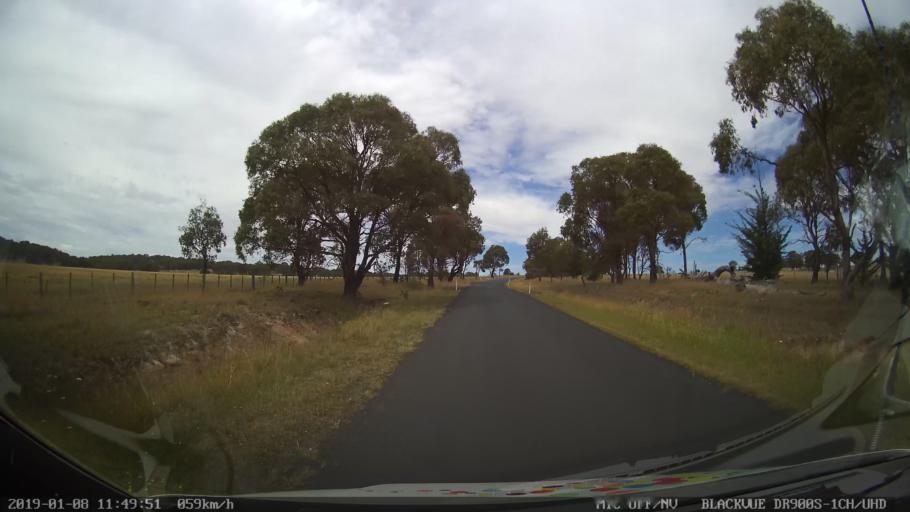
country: AU
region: New South Wales
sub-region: Armidale Dumaresq
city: Armidale
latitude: -30.3774
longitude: 151.5585
